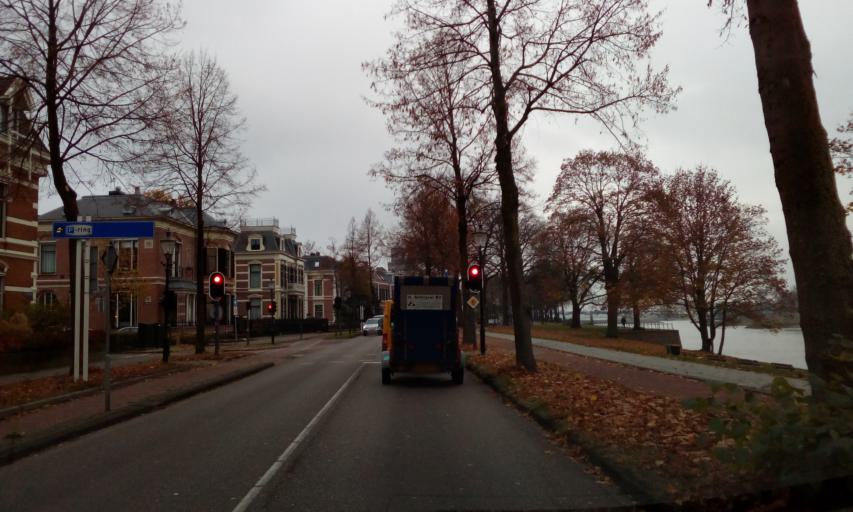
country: NL
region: Overijssel
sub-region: Gemeente Deventer
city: Deventer
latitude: 52.2553
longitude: 6.1485
